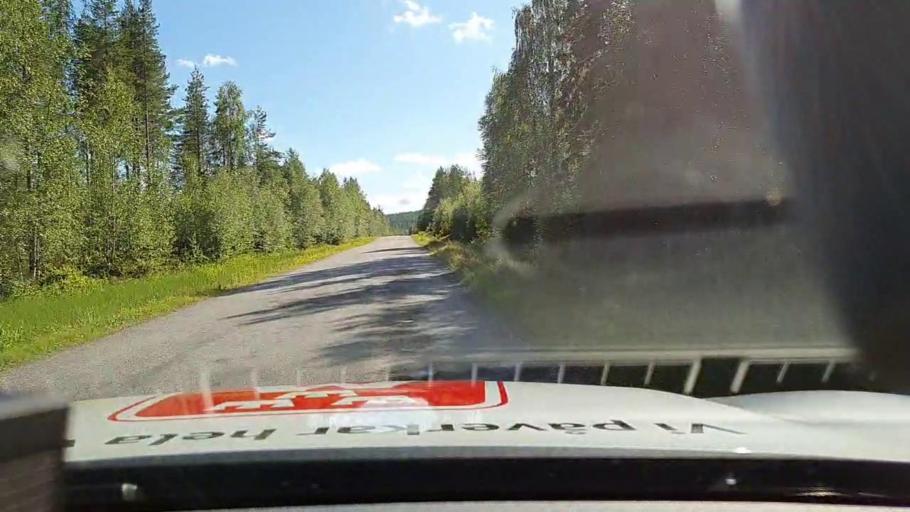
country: SE
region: Norrbotten
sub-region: Overkalix Kommun
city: OEverkalix
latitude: 66.2523
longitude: 23.0141
